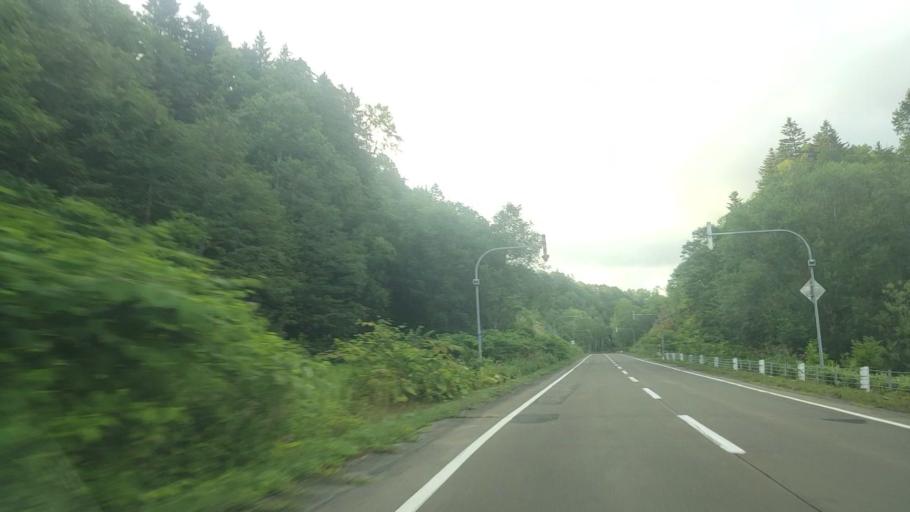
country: JP
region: Hokkaido
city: Bibai
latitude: 43.1309
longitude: 142.0947
